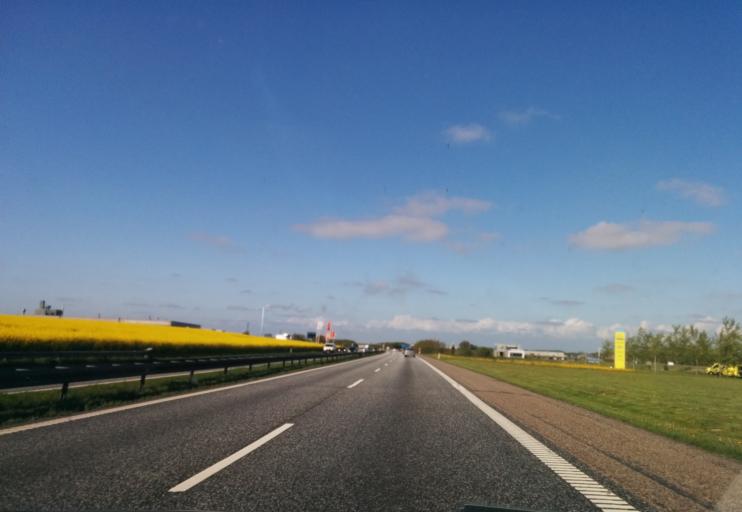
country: DK
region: Central Jutland
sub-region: Hedensted Kommune
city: Hedensted
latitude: 55.7834
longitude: 9.6636
